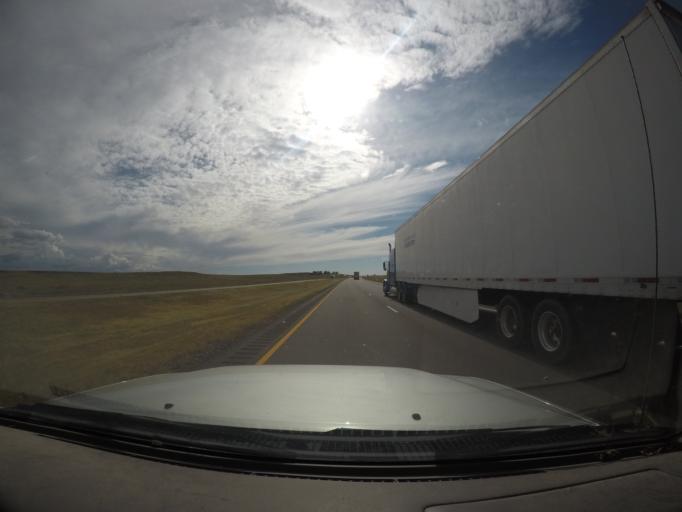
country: US
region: Nebraska
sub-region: Kimball County
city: Kimball
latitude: 41.1907
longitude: -103.8592
